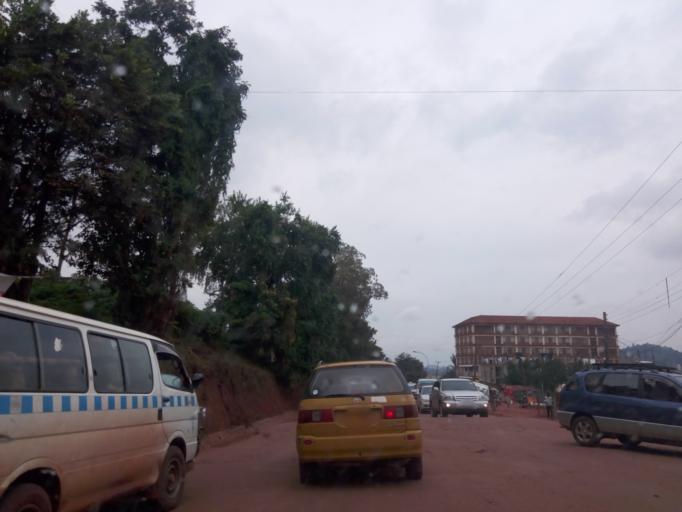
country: UG
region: Central Region
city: Kampala Central Division
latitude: 0.3354
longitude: 32.5637
